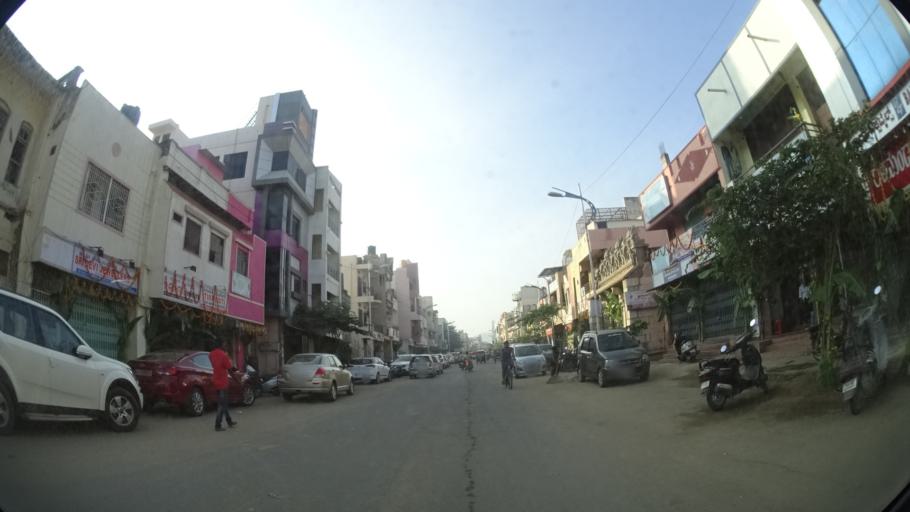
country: IN
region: Karnataka
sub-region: Bellary
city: Hospet
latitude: 15.2705
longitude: 76.3917
